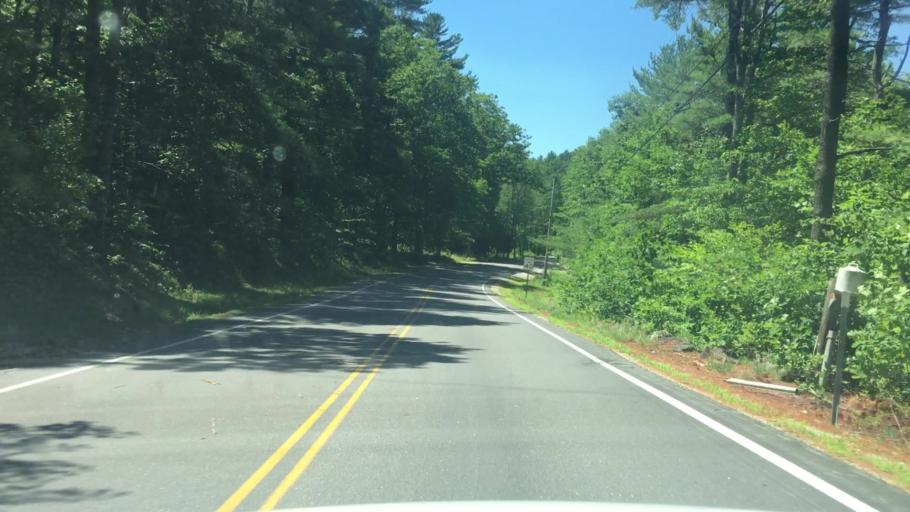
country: US
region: New Hampshire
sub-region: Merrimack County
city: Hopkinton
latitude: 43.1903
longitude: -71.6801
